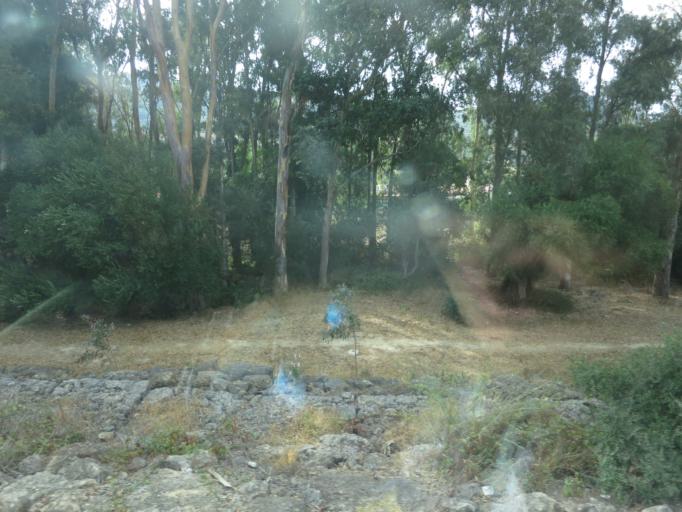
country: ES
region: Andalusia
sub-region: Provincia de Cadiz
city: Algeciras
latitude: 36.0703
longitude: -5.5215
